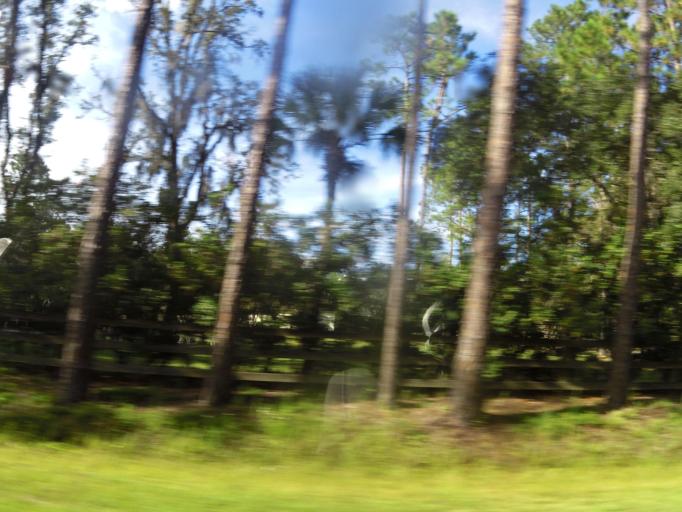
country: US
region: Florida
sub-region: Clay County
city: Green Cove Springs
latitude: 29.9179
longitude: -81.5694
